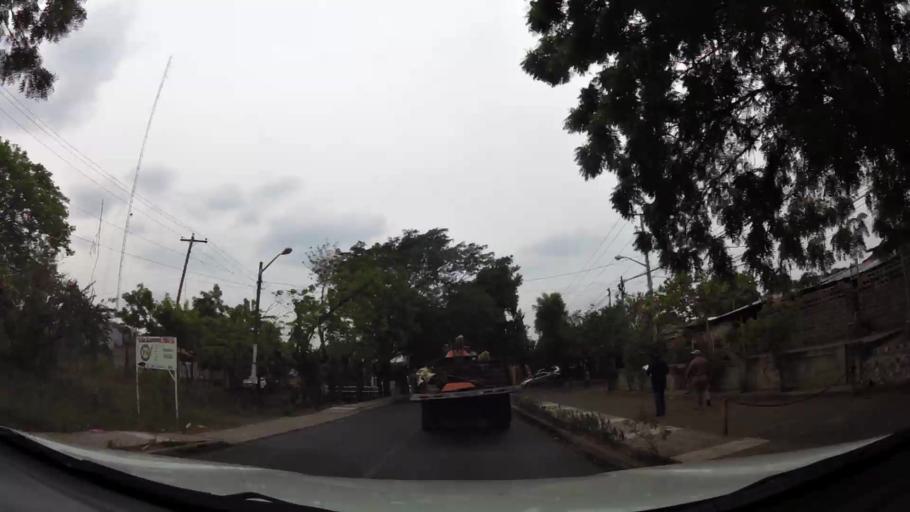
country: NI
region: Leon
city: Leon
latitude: 12.4557
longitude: -86.8691
